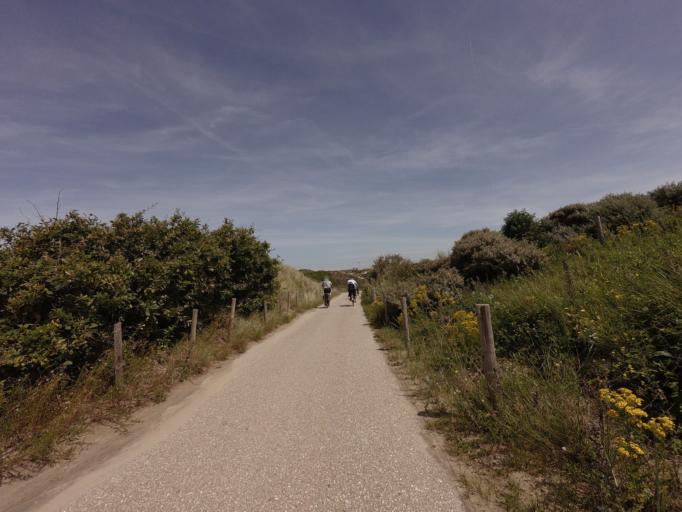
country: NL
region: South Holland
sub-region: Gemeente Den Haag
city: Scheveningen
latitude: 52.0886
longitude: 4.2473
